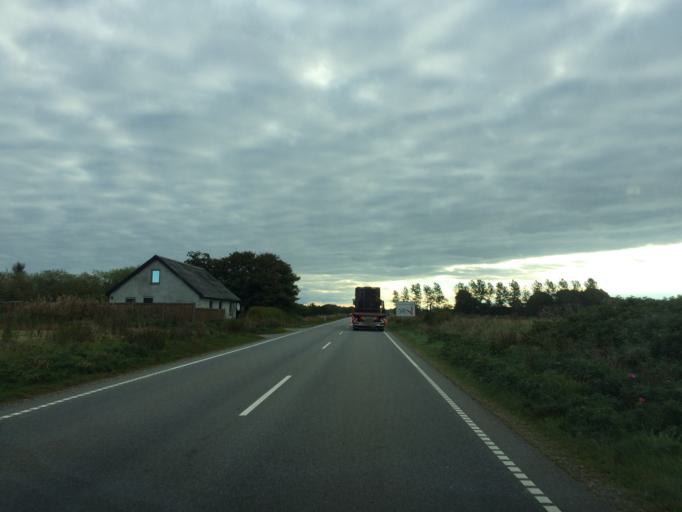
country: DK
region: Central Jutland
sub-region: Ringkobing-Skjern Kommune
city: Tarm
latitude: 55.9671
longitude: 8.5668
